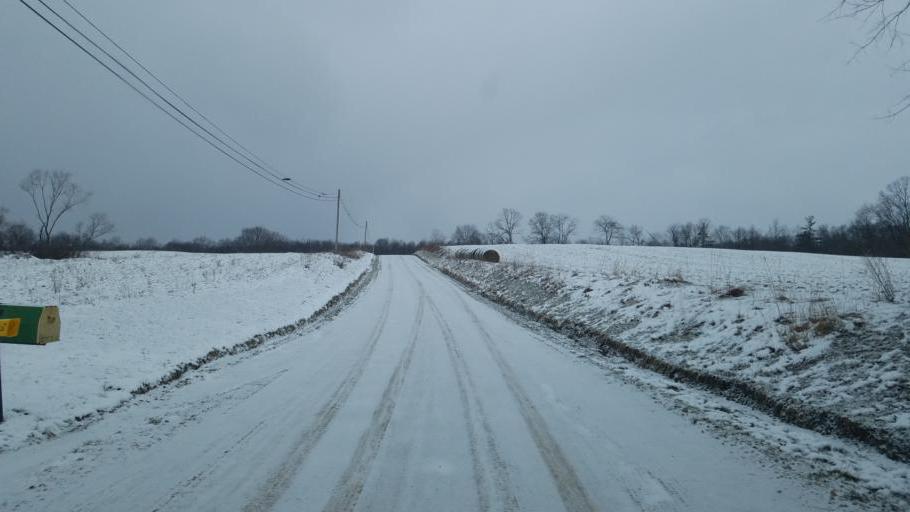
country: US
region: Pennsylvania
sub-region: Venango County
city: Sugarcreek
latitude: 41.4605
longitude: -79.9663
